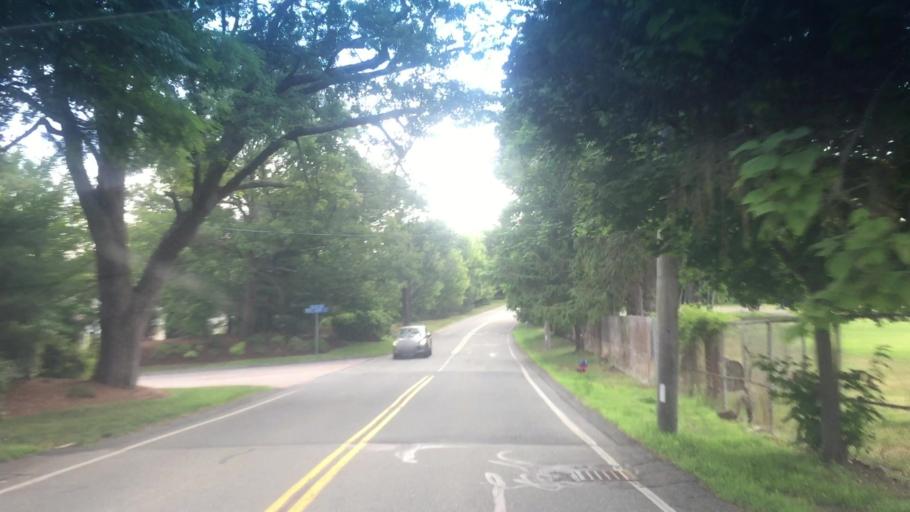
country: US
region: Massachusetts
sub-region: Norfolk County
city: Walpole
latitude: 42.1604
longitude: -71.2212
